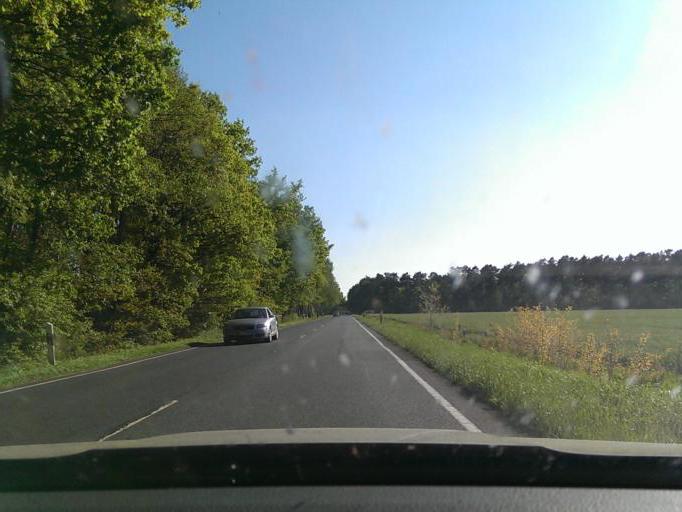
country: DE
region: Lower Saxony
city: Wietze
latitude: 52.5773
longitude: 9.8664
